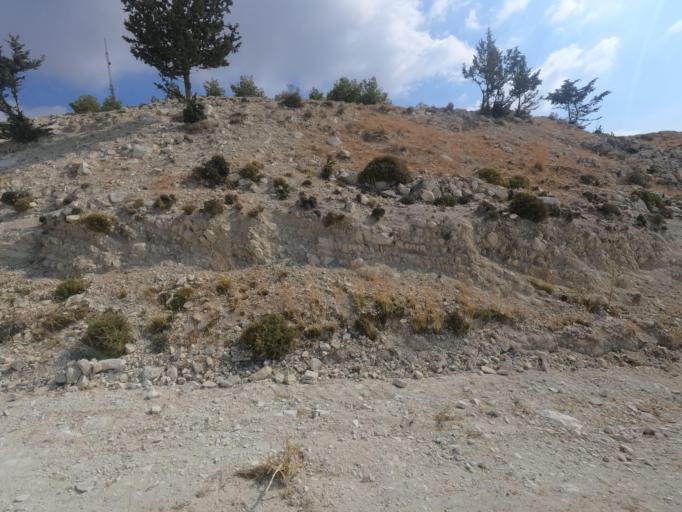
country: CY
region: Larnaka
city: Psevdas
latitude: 34.9488
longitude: 33.5137
